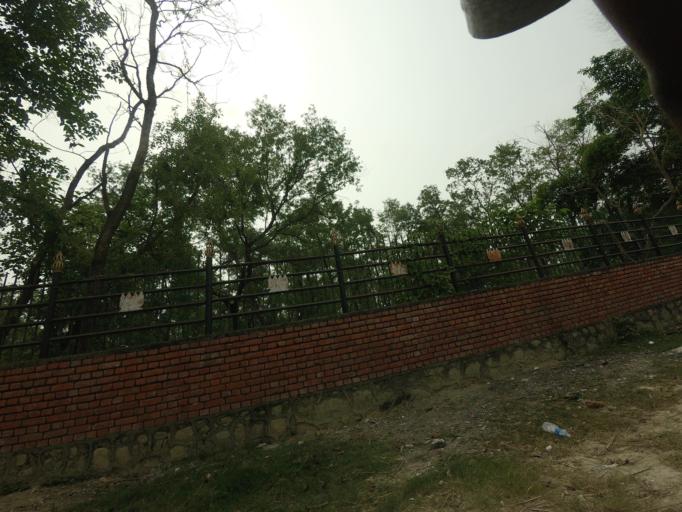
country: IN
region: Uttar Pradesh
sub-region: Maharajganj
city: Nautanwa
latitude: 27.4873
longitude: 83.2680
